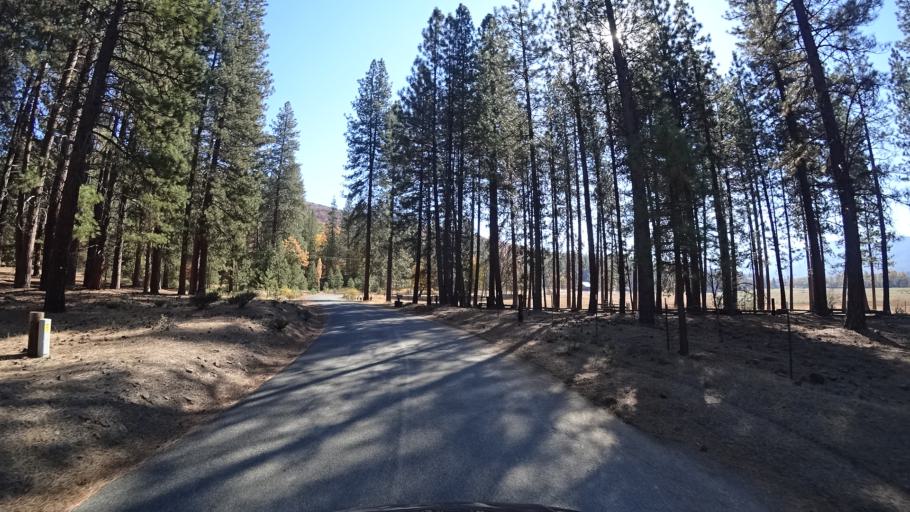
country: US
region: California
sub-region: Siskiyou County
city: Yreka
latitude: 41.5902
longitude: -122.9576
